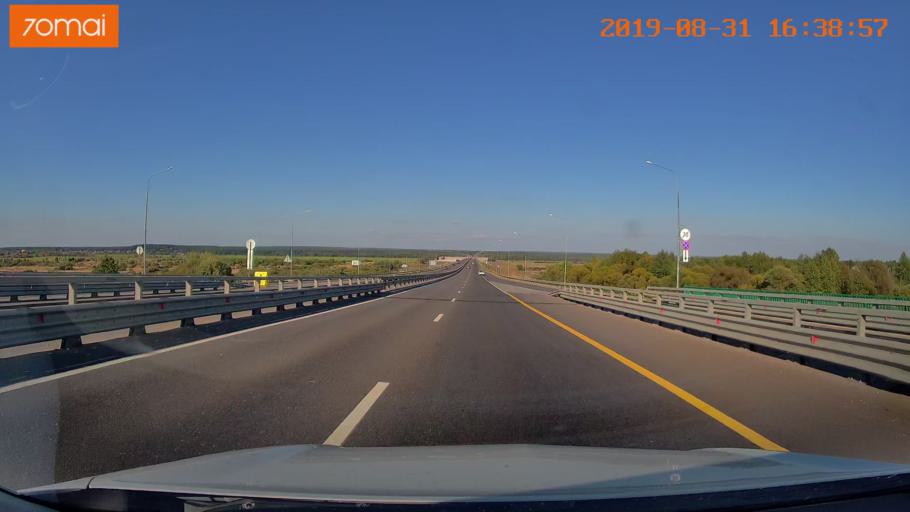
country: RU
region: Kaluga
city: Kurovskoye
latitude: 54.5453
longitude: 36.0154
